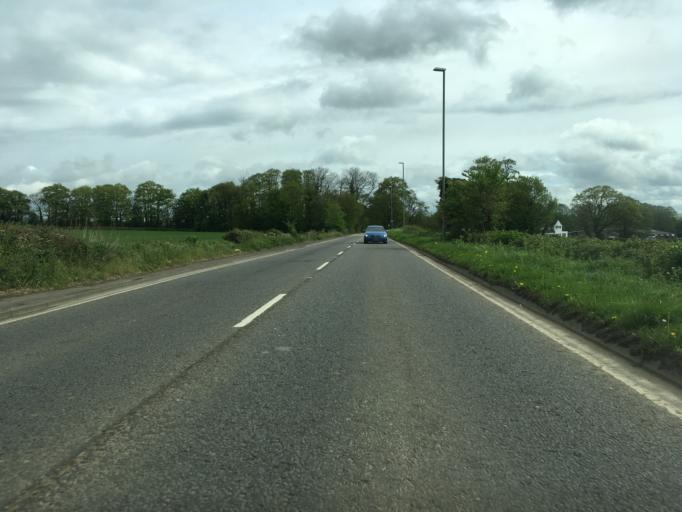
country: GB
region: England
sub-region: Bath and North East Somerset
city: Camerton
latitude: 51.3061
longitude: -2.4458
